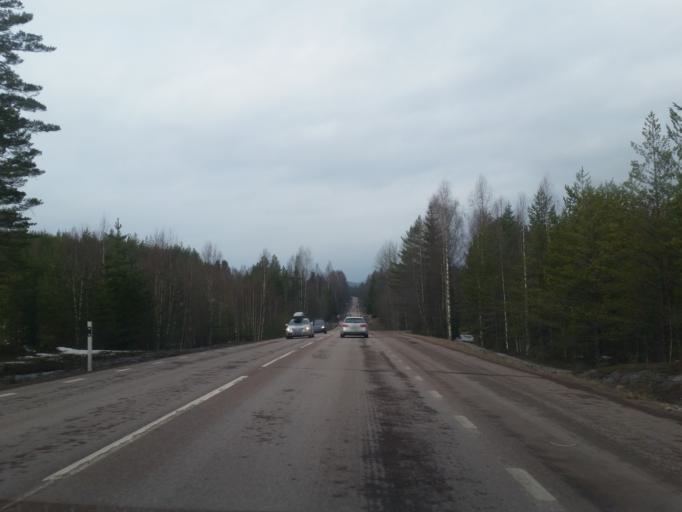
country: SE
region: Dalarna
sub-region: Mora Kommun
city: Mora
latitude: 61.0626
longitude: 14.3986
